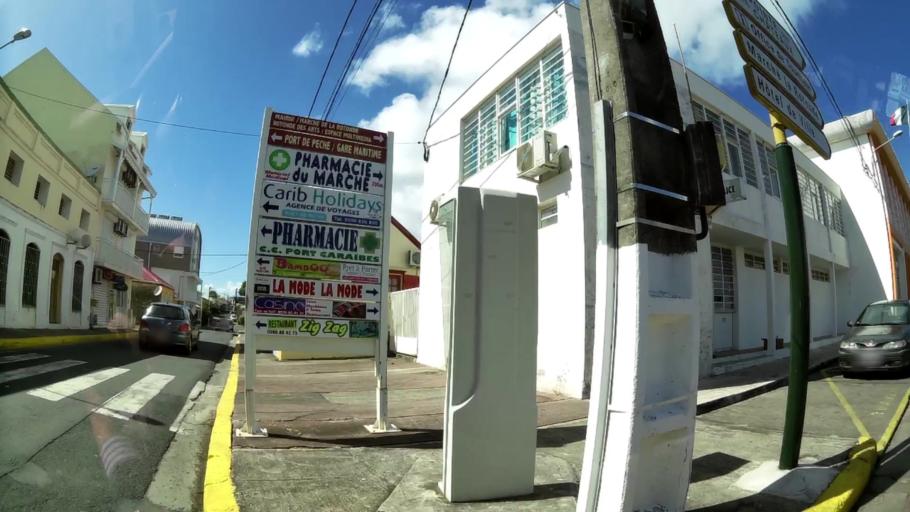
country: GP
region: Guadeloupe
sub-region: Guadeloupe
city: Saint-Francois
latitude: 16.2512
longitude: -61.2740
